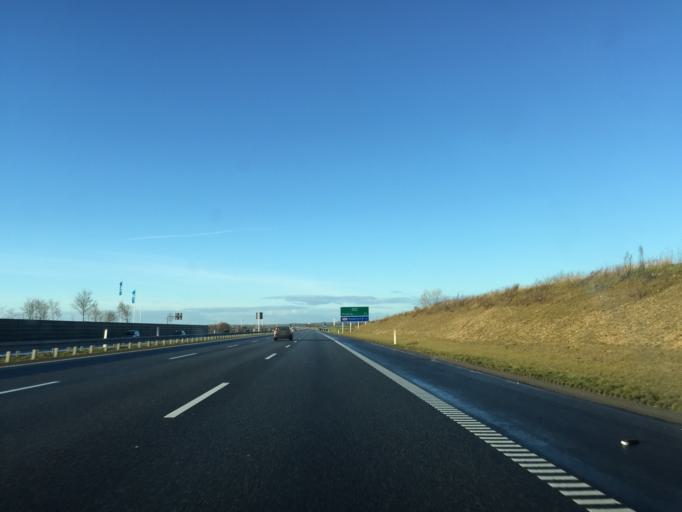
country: DK
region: South Denmark
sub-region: Middelfart Kommune
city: Norre Aby
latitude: 55.4785
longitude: 9.8801
